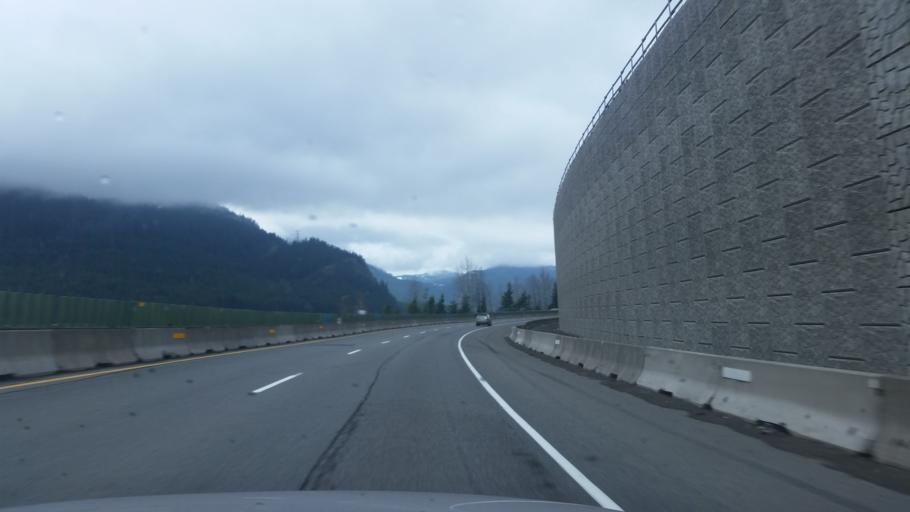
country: US
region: Washington
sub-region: King County
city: Tanner
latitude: 47.3417
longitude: -121.3626
